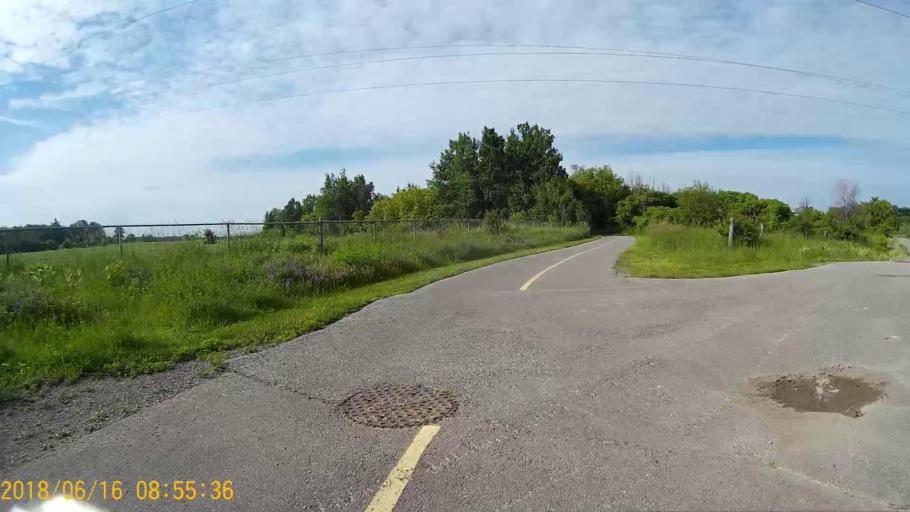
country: CA
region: Ontario
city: Bells Corners
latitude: 45.3310
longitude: -75.8882
